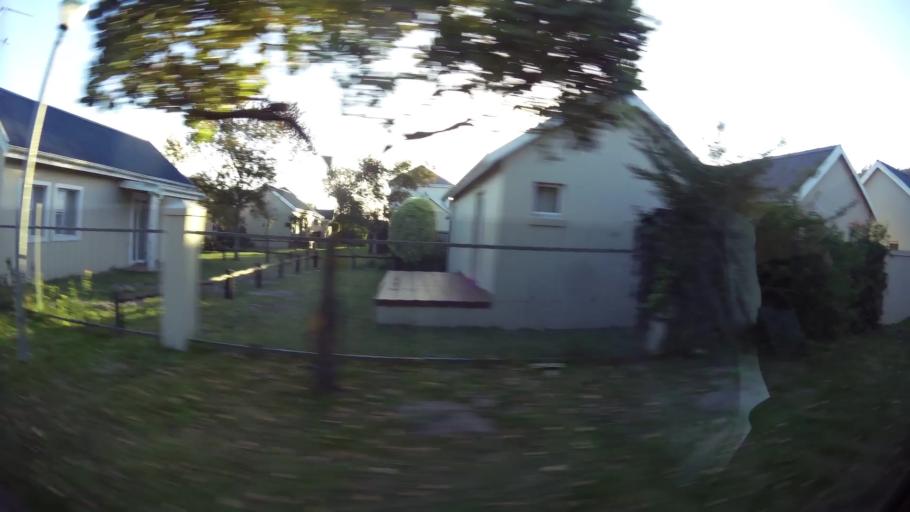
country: ZA
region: Western Cape
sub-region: Eden District Municipality
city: Knysna
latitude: -34.0123
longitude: 22.7944
